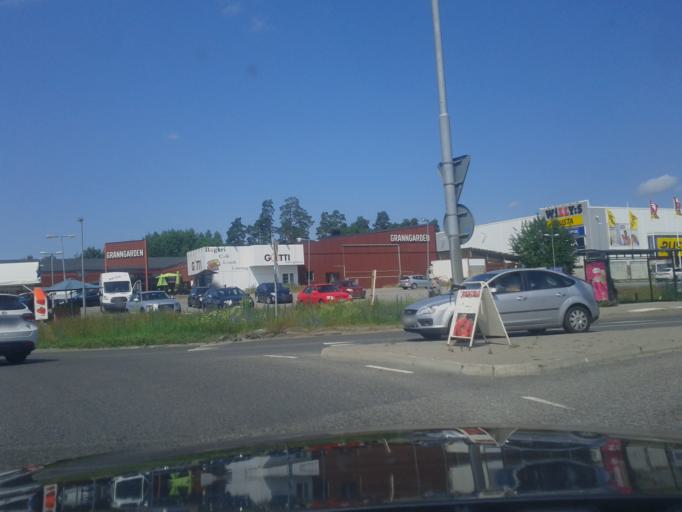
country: SE
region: Stockholm
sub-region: Taby Kommun
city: Taby
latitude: 59.4623
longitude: 18.1321
